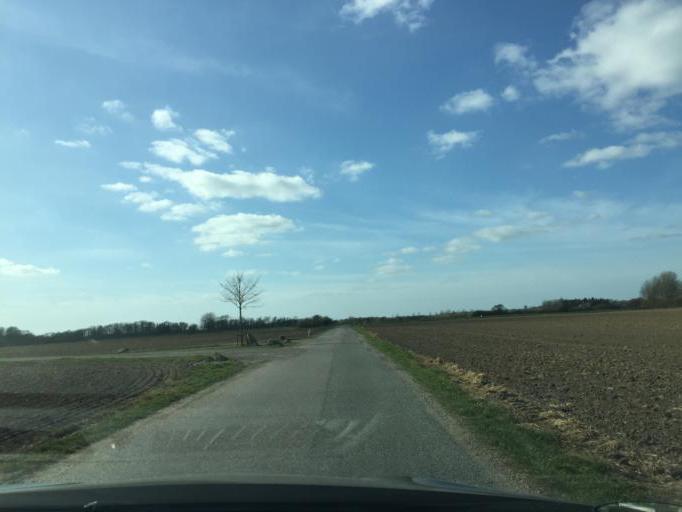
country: DK
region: South Denmark
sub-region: Kerteminde Kommune
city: Langeskov
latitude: 55.3128
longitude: 10.5640
